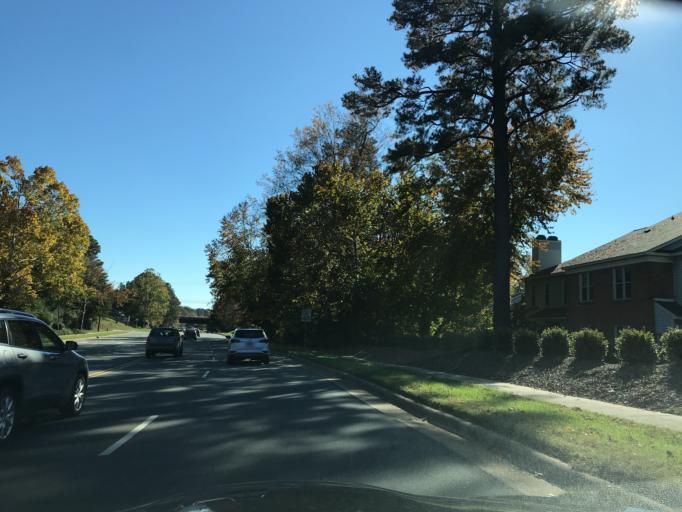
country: US
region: North Carolina
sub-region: Wake County
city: Raleigh
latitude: 35.8586
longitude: -78.6013
